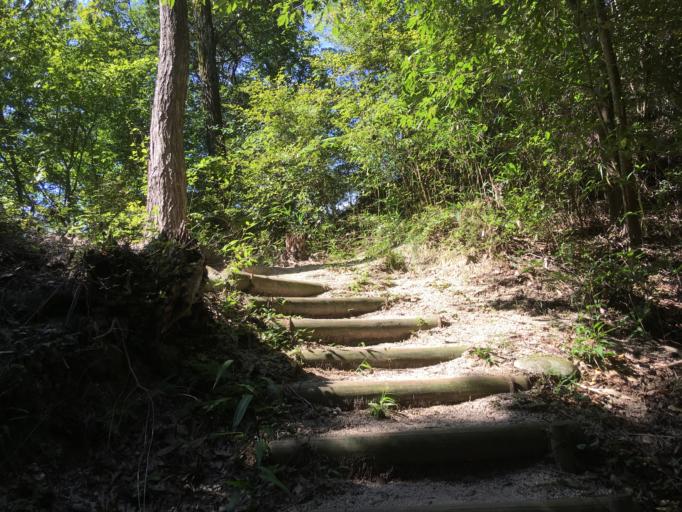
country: JP
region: Nara
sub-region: Ikoma-shi
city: Ikoma
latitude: 34.7434
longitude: 135.6860
